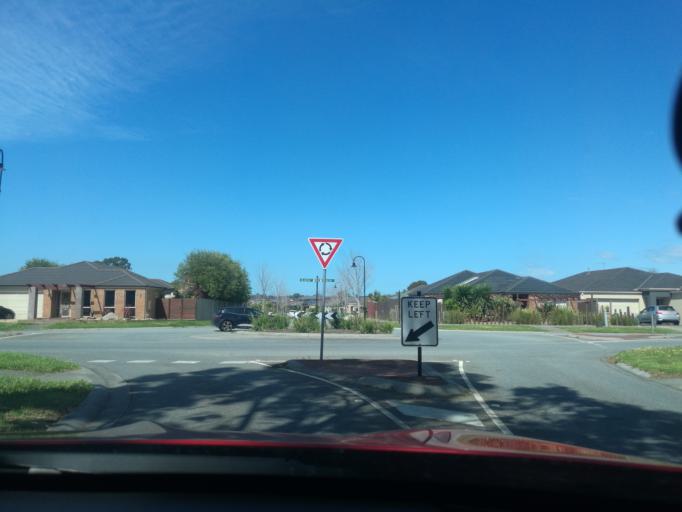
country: AU
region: Victoria
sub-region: Casey
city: Lynbrook
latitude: -38.0656
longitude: 145.2467
